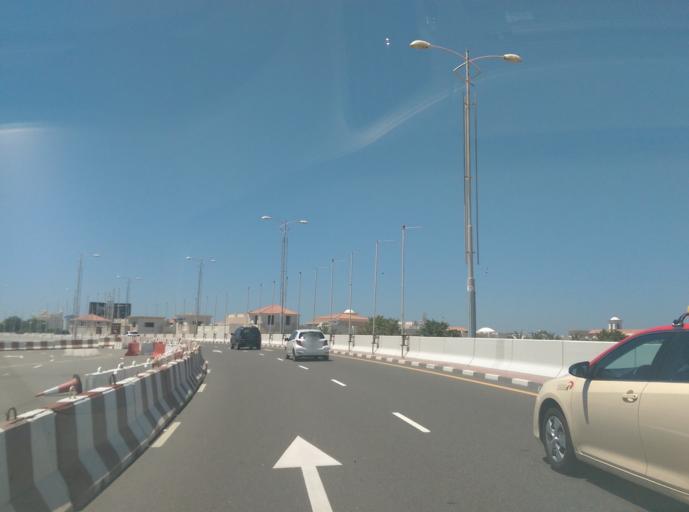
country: AE
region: Dubai
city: Dubai
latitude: 25.0998
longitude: 55.1621
